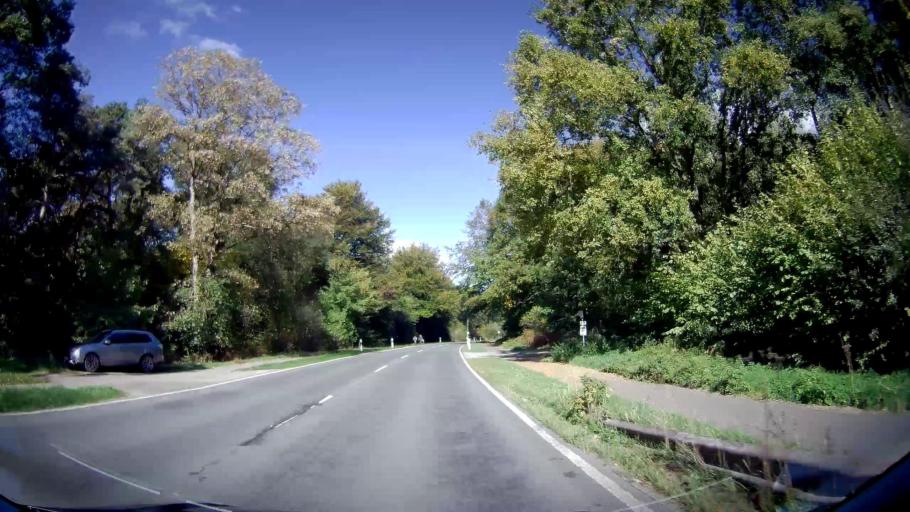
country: DE
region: North Rhine-Westphalia
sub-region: Regierungsbezirk Dusseldorf
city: Hunxe
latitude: 51.6203
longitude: 6.7550
